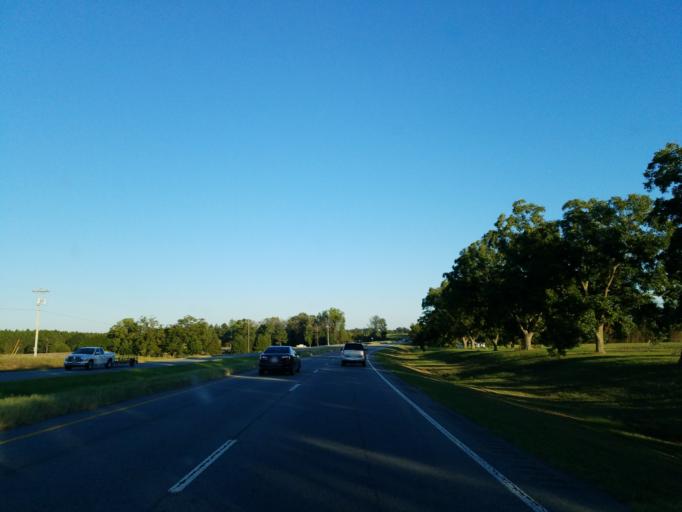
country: US
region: Georgia
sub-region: Worth County
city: Sylvester
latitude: 31.5027
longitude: -83.7196
